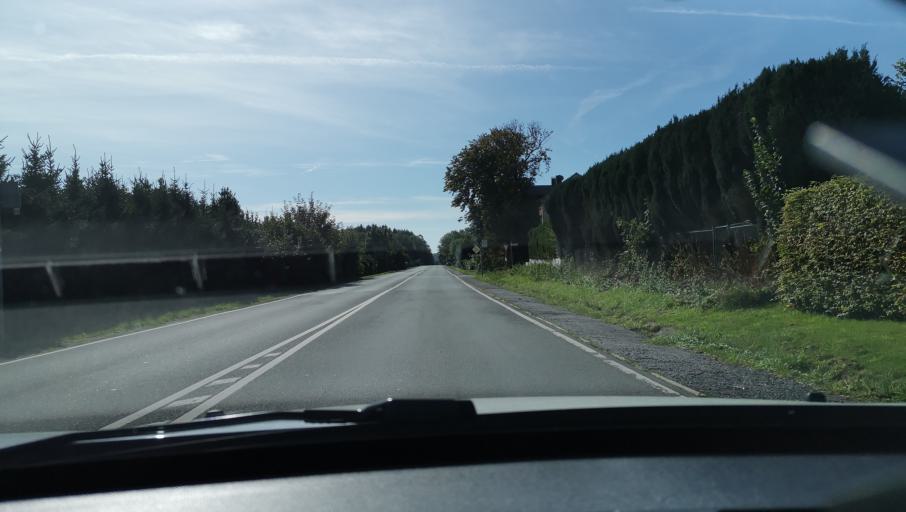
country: DE
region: North Rhine-Westphalia
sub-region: Regierungsbezirk Arnsberg
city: Breckerfeld
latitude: 51.2431
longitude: 7.4662
